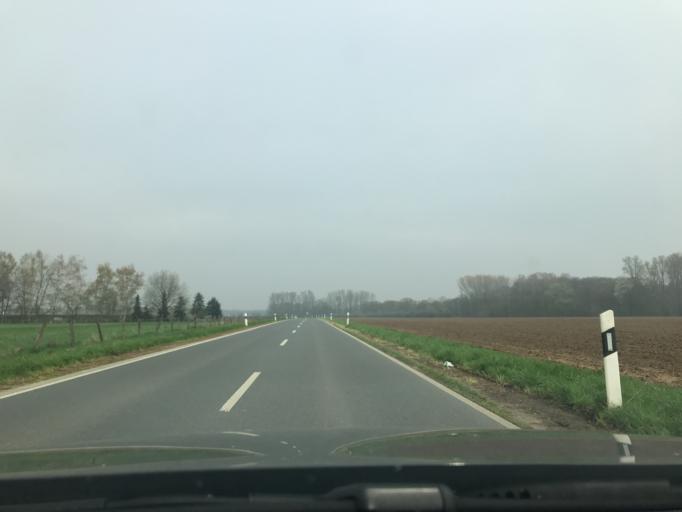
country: DE
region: North Rhine-Westphalia
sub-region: Regierungsbezirk Dusseldorf
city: Wachtendonk
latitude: 51.4311
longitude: 6.3468
